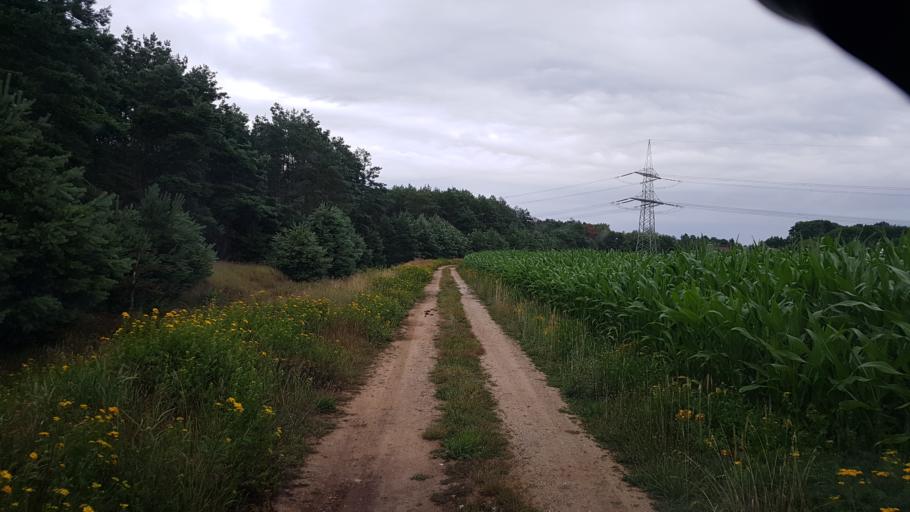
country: DE
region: Brandenburg
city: Schilda
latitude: 51.6385
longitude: 13.3634
